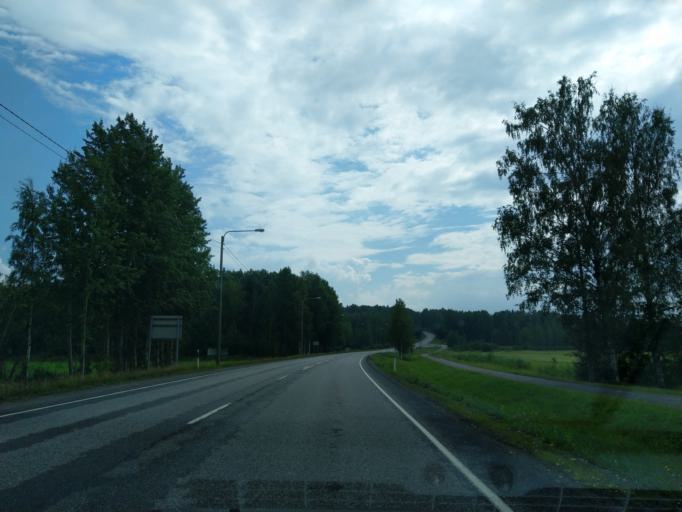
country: FI
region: South Karelia
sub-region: Imatra
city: Parikkala
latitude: 61.5751
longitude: 29.5043
